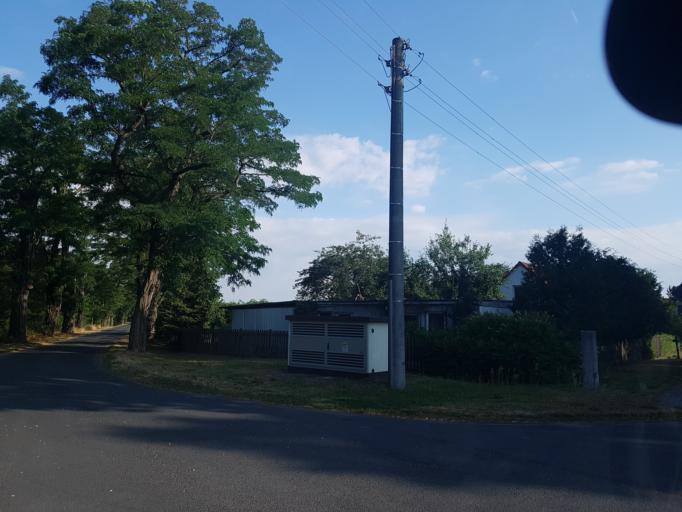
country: DE
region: Saxony-Anhalt
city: Seyda
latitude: 51.9234
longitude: 12.9188
